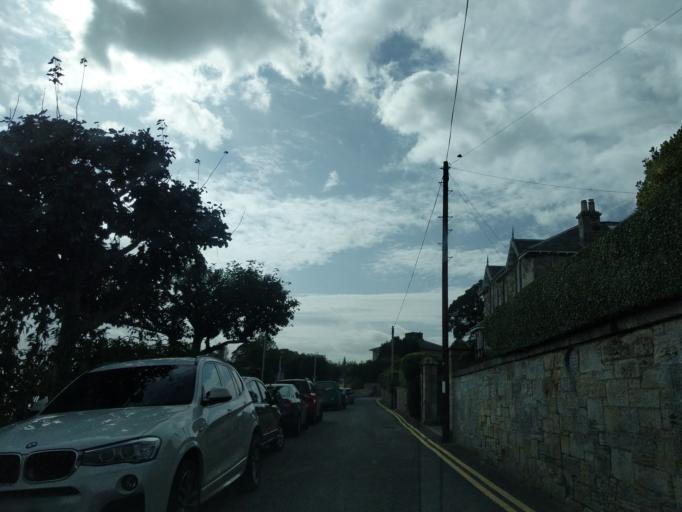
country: GB
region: Scotland
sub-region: Fife
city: Aberdour
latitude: 56.0518
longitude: -3.2962
